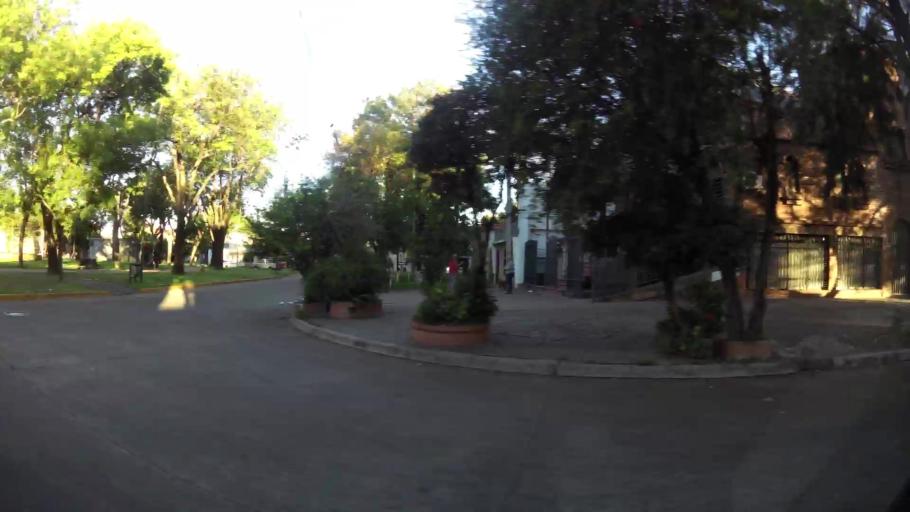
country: AR
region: Santa Fe
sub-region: Departamento de Rosario
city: Rosario
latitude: -32.9704
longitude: -60.6709
